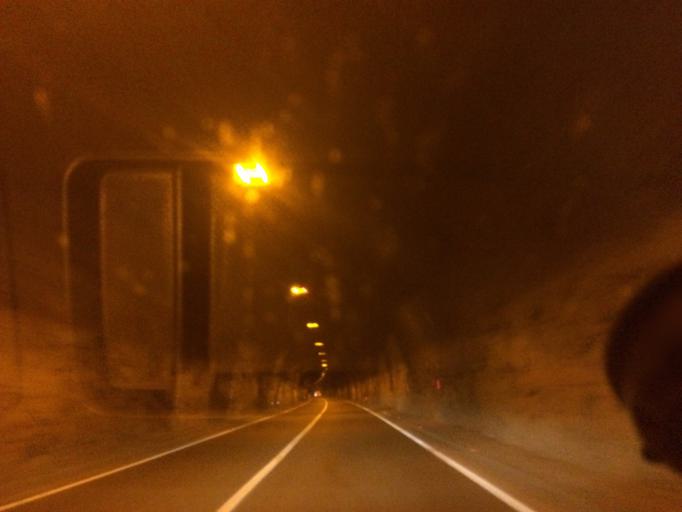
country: MK
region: Demir Kapija
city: Demir Kapija
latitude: 41.4069
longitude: 22.2596
